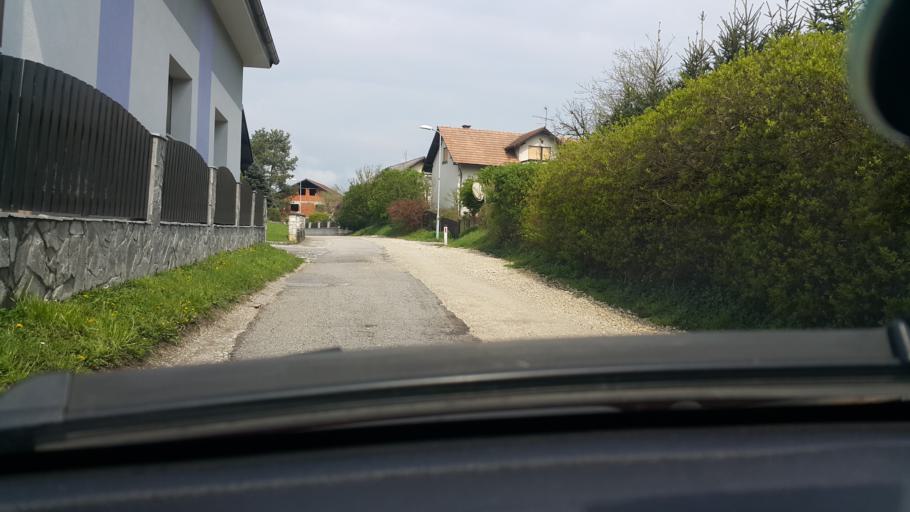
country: SI
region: Brezice
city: Brezice
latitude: 45.9059
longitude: 15.6509
